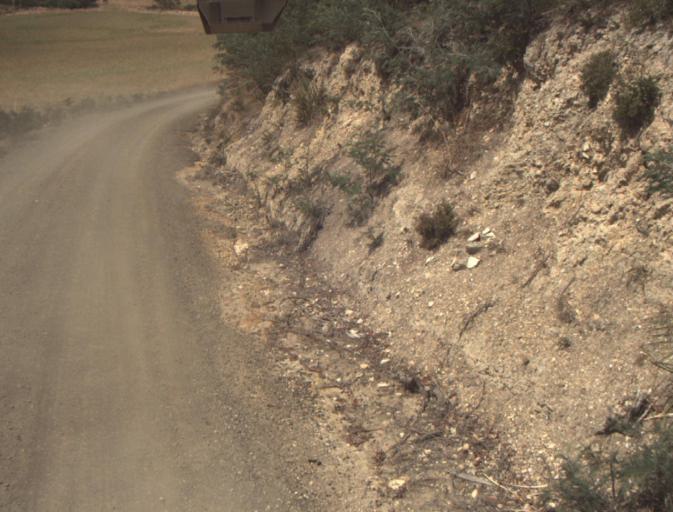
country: AU
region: Tasmania
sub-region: Launceston
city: Mayfield
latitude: -41.2105
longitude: 147.1422
